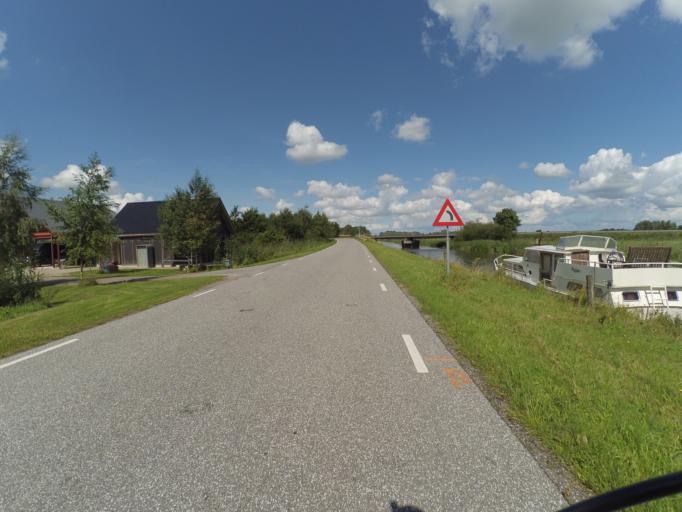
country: NL
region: Friesland
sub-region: Gemeente Kollumerland en Nieuwkruisland
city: Kollum
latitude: 53.2556
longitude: 6.1787
